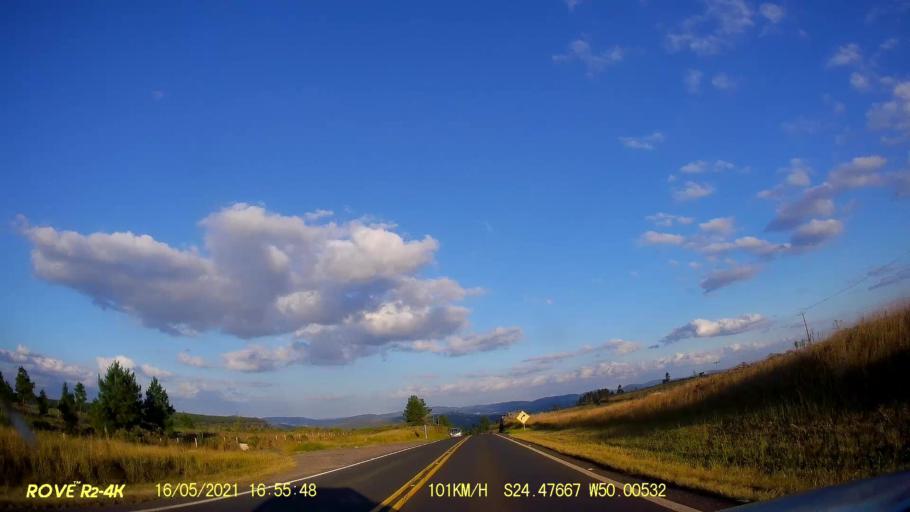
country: BR
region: Parana
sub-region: Pirai Do Sul
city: Pirai do Sul
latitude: -24.4762
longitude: -50.0055
